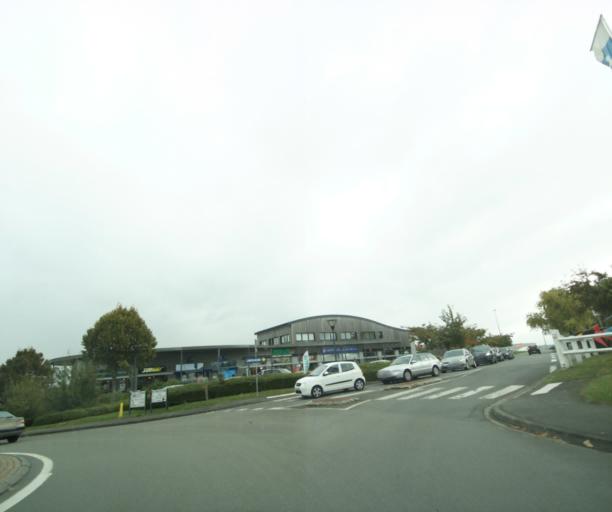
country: FR
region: Nord-Pas-de-Calais
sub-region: Departement du Nord
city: Bondues
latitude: 50.6934
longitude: 3.0889
